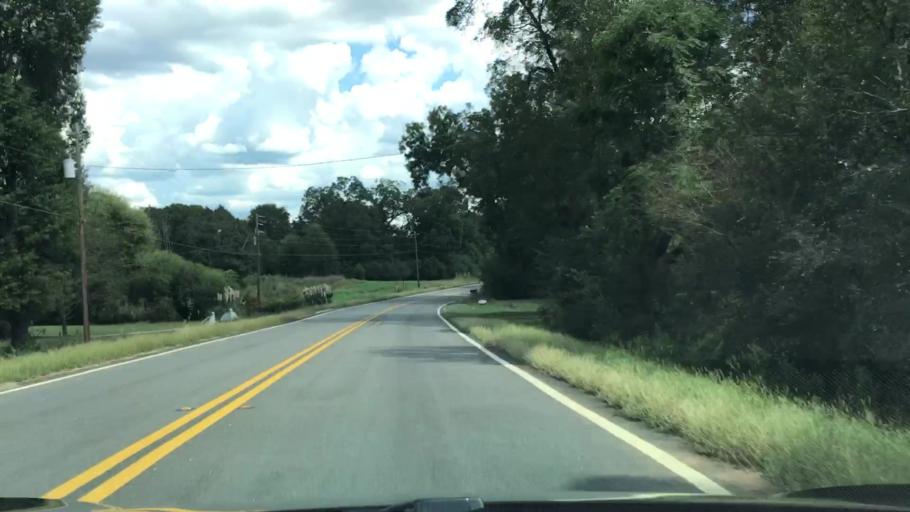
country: US
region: Georgia
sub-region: Greene County
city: Greensboro
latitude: 33.5655
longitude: -83.1488
